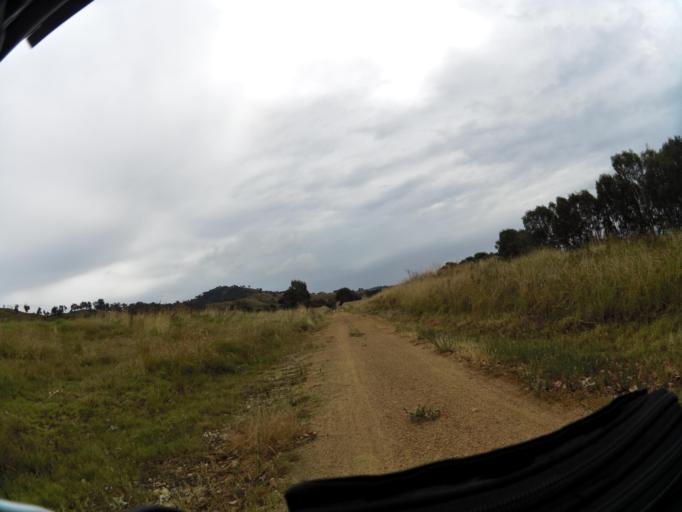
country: AU
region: New South Wales
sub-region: Albury Municipality
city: East Albury
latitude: -36.2177
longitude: 147.0620
